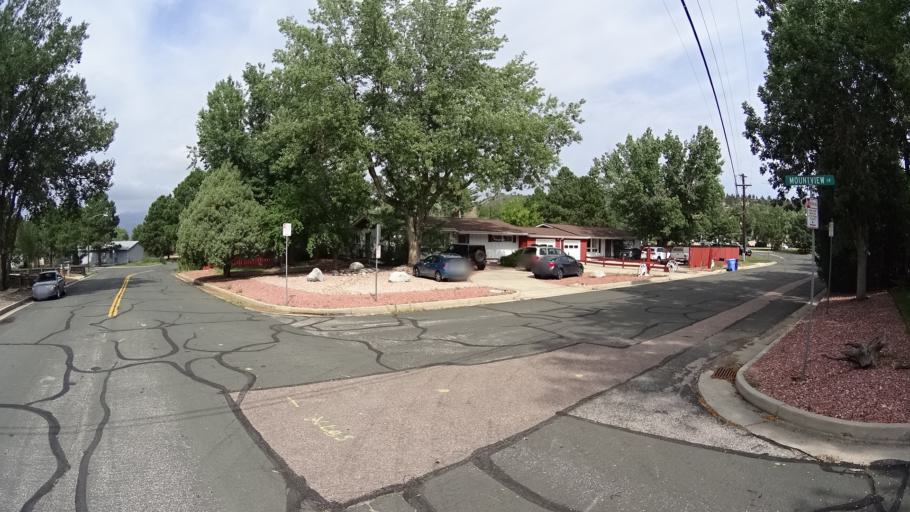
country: US
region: Colorado
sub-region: El Paso County
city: Colorado Springs
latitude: 38.8889
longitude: -104.7969
